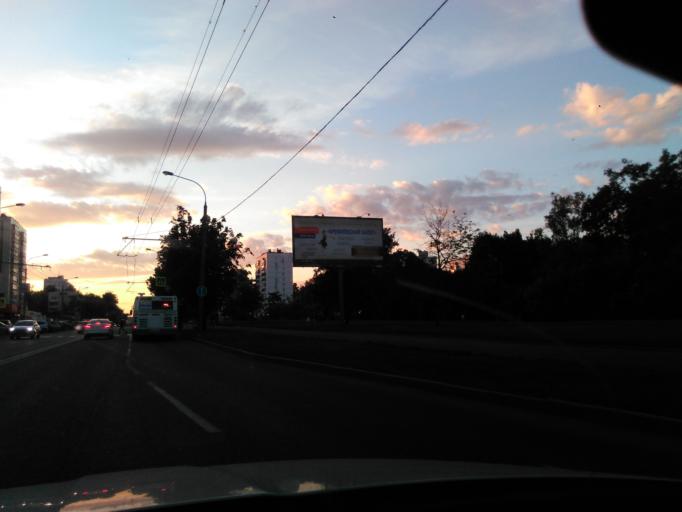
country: RU
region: Moscow
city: Zapadnoye Degunino
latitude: 55.8763
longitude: 37.5249
